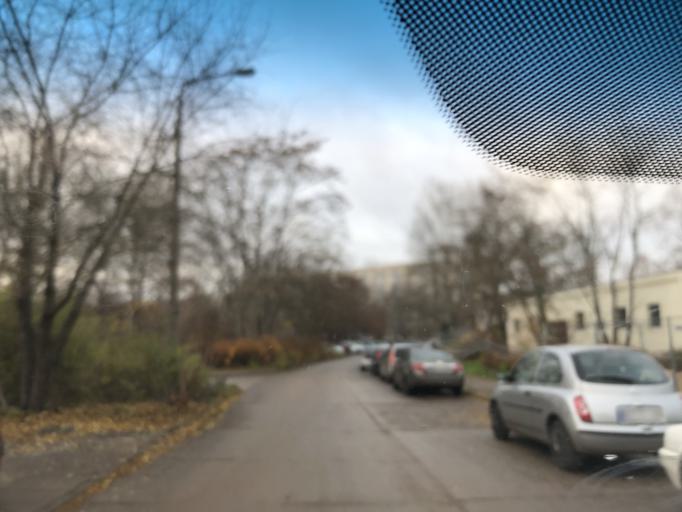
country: DE
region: Saxony-Anhalt
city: Halle Neustadt
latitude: 51.4717
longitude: 11.9174
